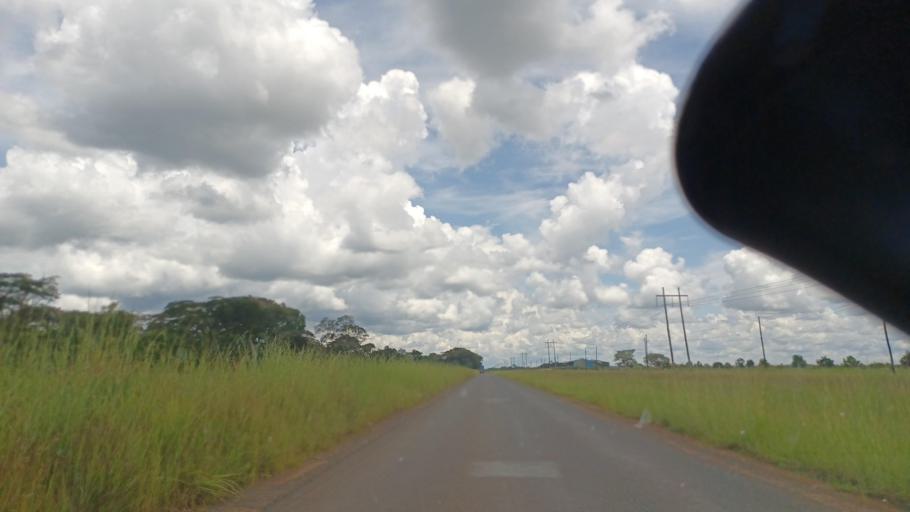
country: ZM
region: North-Western
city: Solwezi
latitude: -12.4428
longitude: 26.2083
